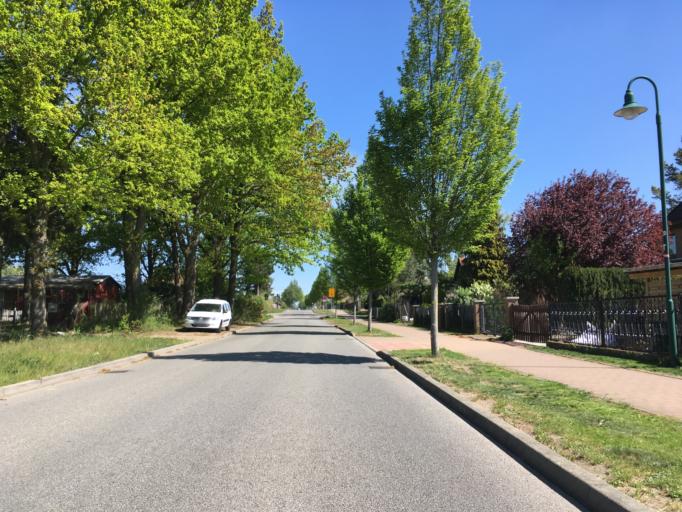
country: DE
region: Berlin
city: Buch
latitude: 52.6589
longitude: 13.5206
